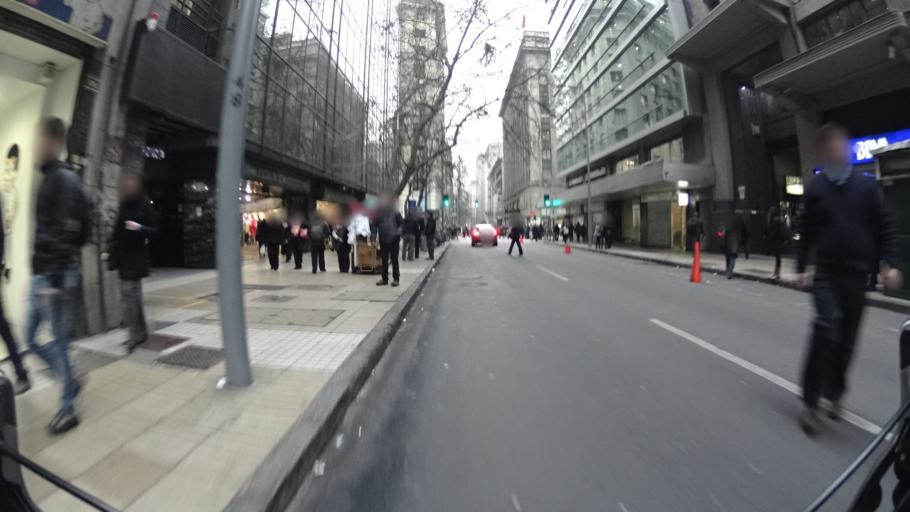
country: CL
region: Santiago Metropolitan
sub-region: Provincia de Santiago
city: Santiago
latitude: -33.4417
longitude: -70.6492
